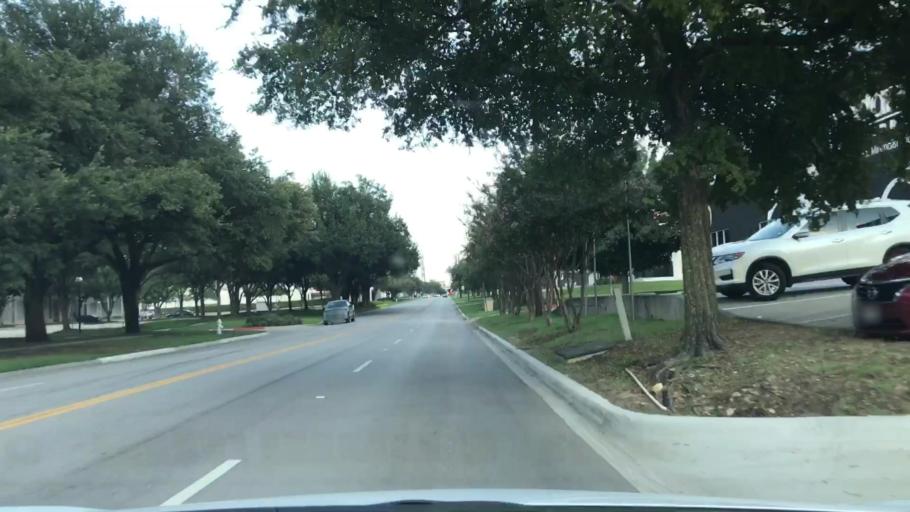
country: US
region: Texas
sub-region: Dallas County
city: Addison
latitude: 32.9331
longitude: -96.8296
